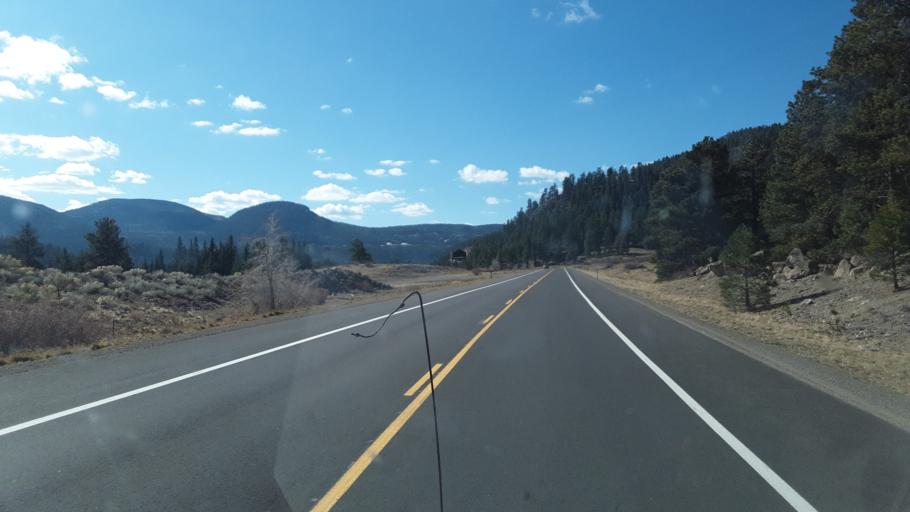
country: US
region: Colorado
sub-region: Rio Grande County
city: Del Norte
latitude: 37.6381
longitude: -106.6689
